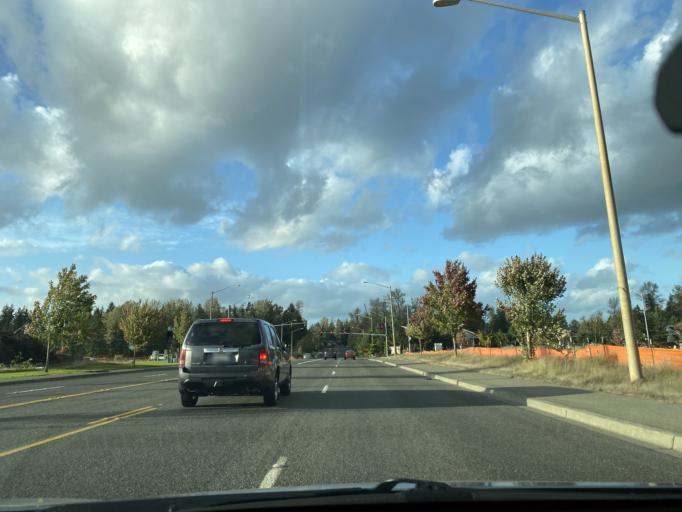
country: US
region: Washington
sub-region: Pierce County
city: South Hill
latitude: 47.0970
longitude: -122.2647
